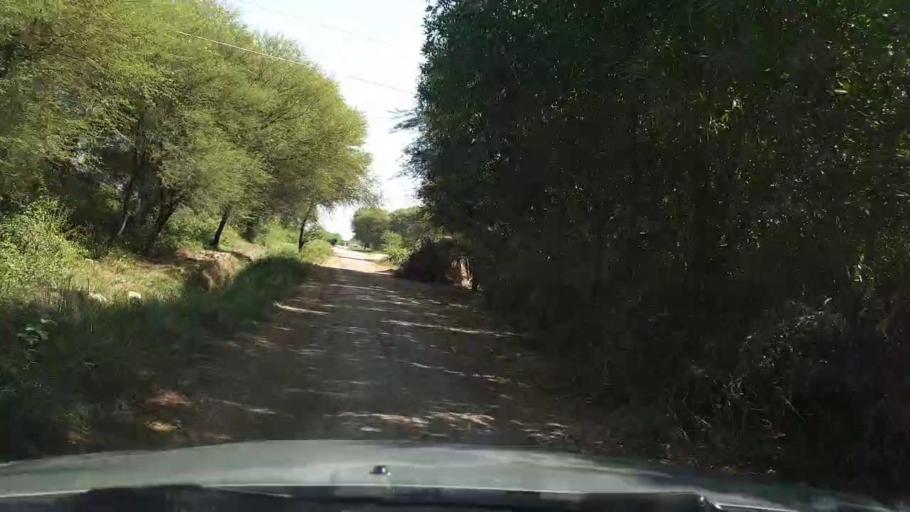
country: PK
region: Sindh
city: Bulri
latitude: 25.0198
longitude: 68.3098
